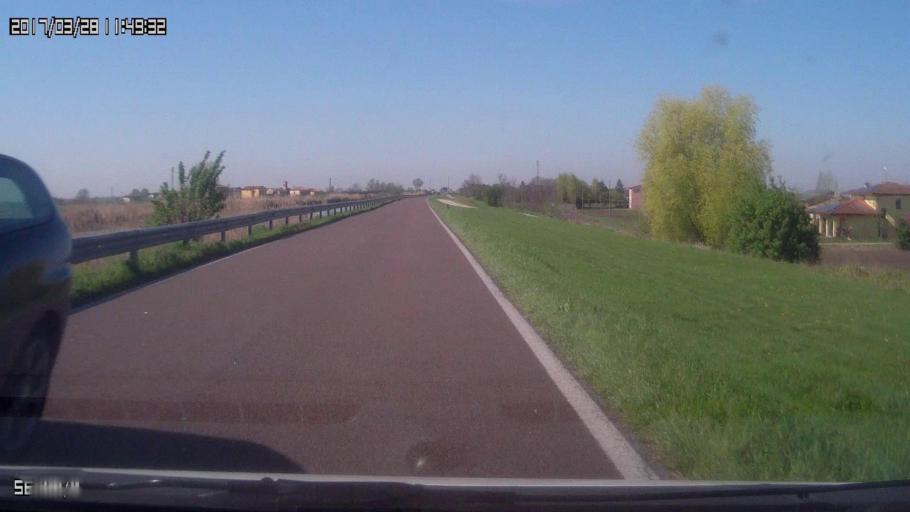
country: IT
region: Veneto
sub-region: Provincia di Venezia
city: Sant'Anna
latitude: 45.1566
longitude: 12.2118
